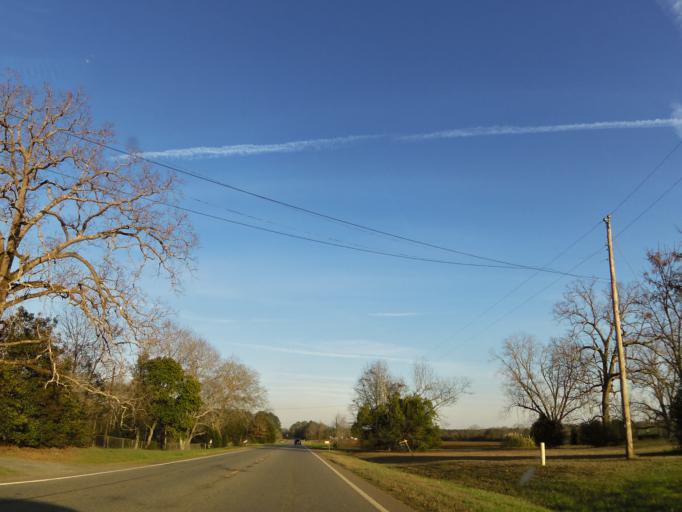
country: US
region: Georgia
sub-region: Sumter County
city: Americus
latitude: 32.0557
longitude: -84.2896
